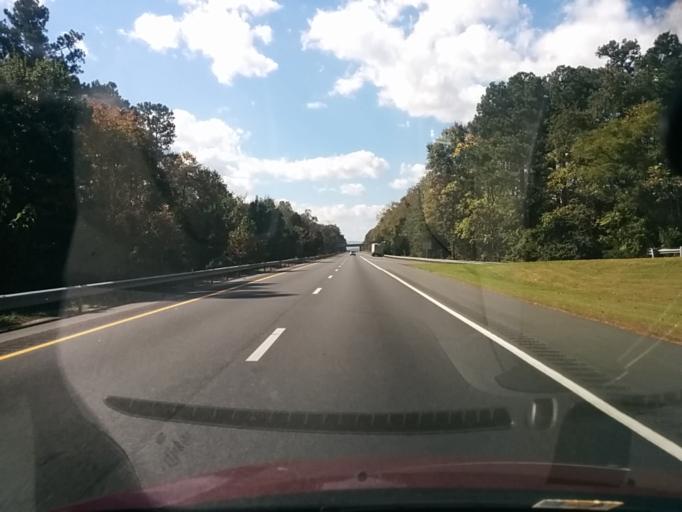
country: US
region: Virginia
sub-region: Albemarle County
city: Crozet
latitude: 38.0340
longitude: -78.6303
